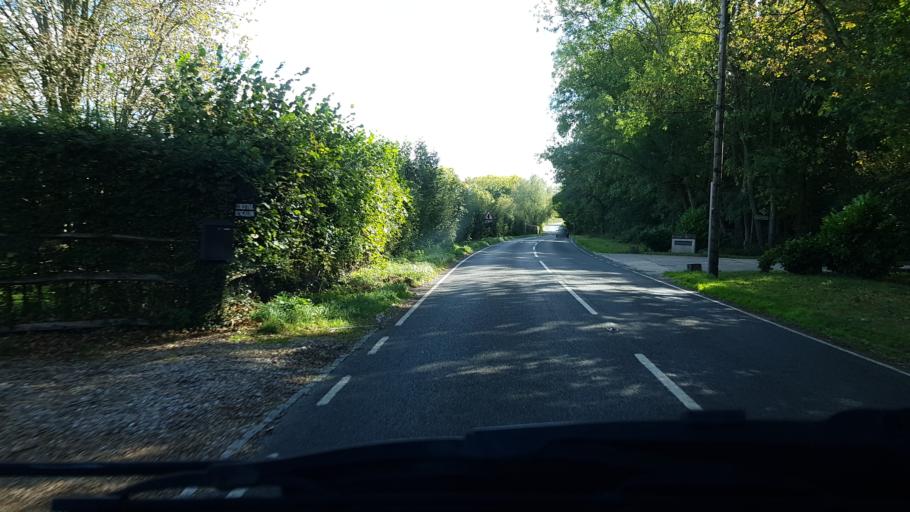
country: GB
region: England
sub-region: West Sussex
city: Billingshurst
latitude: 50.9951
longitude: -0.4544
